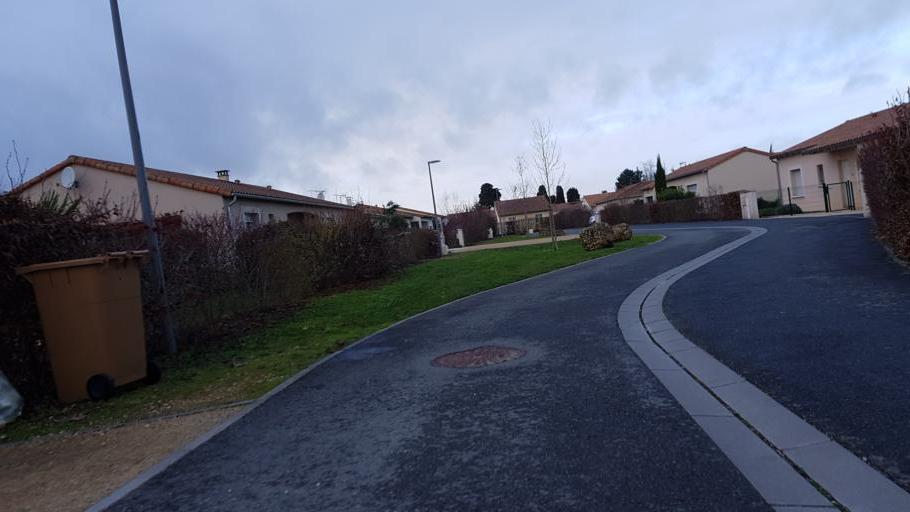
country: FR
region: Poitou-Charentes
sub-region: Departement de la Vienne
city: Avanton
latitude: 46.6620
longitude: 0.3094
